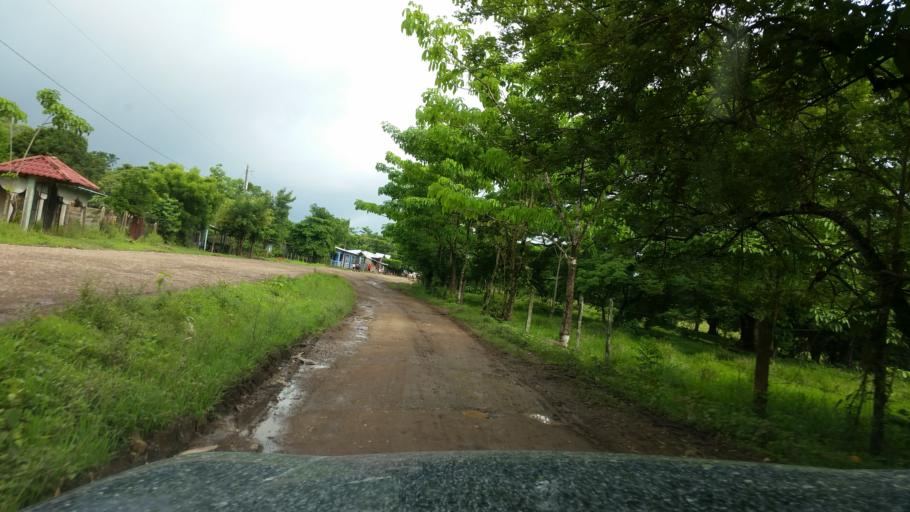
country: NI
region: Atlantico Norte (RAAN)
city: Siuna
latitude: 13.4318
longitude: -84.8531
